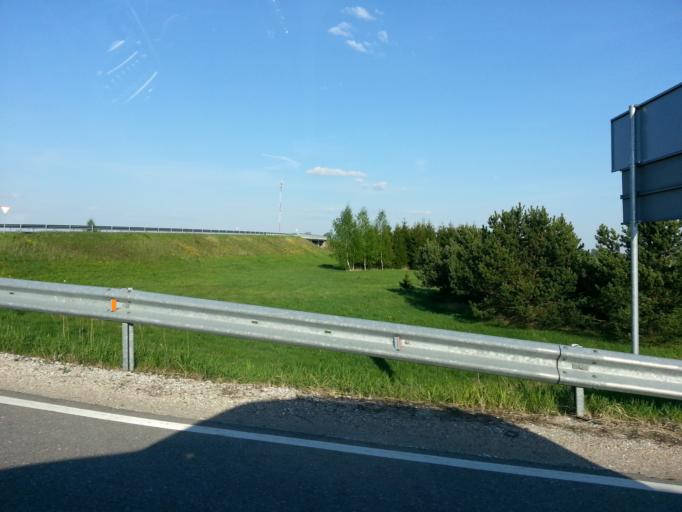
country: LT
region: Vilnius County
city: Ukmerge
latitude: 55.3977
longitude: 24.6976
